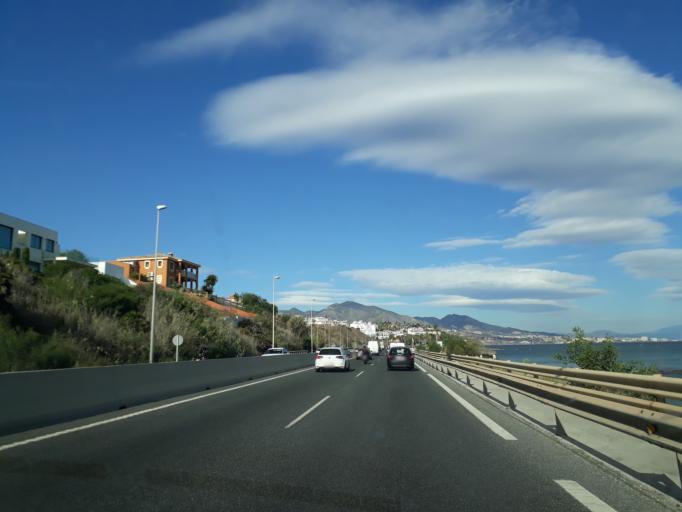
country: ES
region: Andalusia
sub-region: Provincia de Malaga
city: Fuengirola
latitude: 36.5096
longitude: -4.6365
